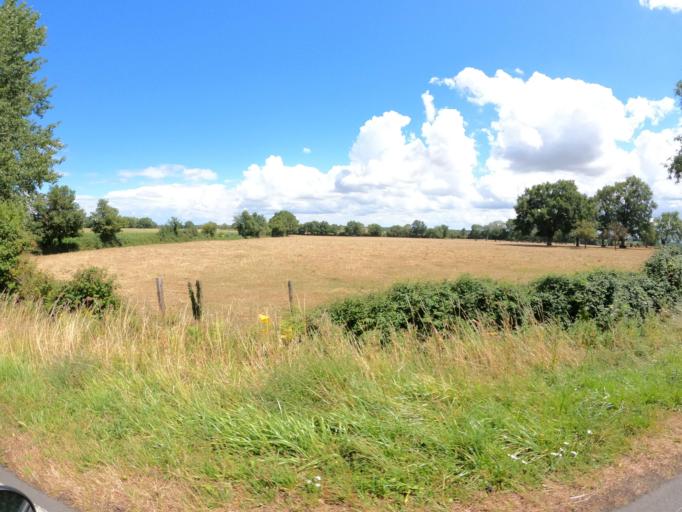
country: FR
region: Pays de la Loire
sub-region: Departement de la Sarthe
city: Brulon
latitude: 47.9338
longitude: -0.2593
